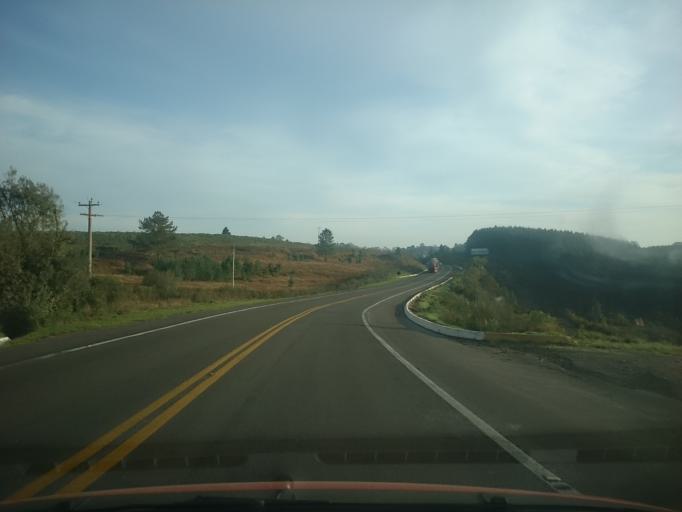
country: BR
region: Rio Grande do Sul
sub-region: Vacaria
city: Vacaria
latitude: -28.2921
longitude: -50.8024
